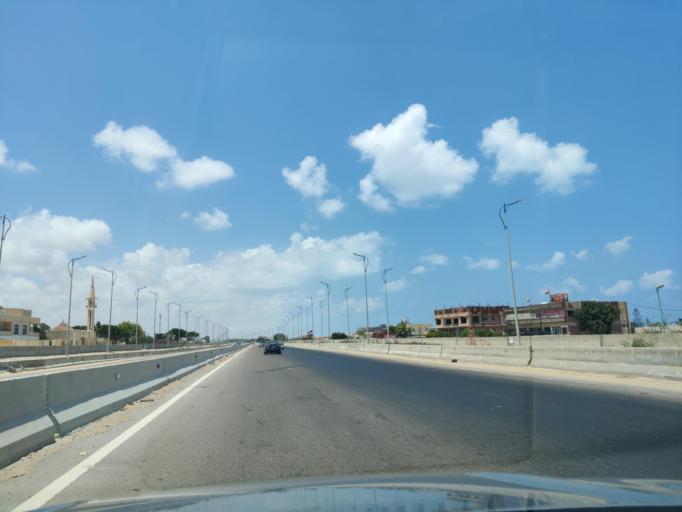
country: EG
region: Alexandria
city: Alexandria
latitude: 30.9606
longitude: 29.5429
